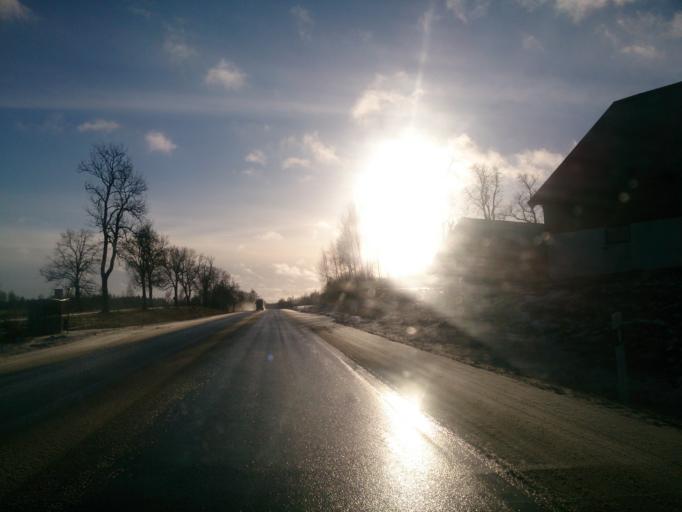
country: SE
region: OEstergoetland
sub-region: Atvidabergs Kommun
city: Atvidaberg
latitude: 58.2286
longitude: 15.9657
